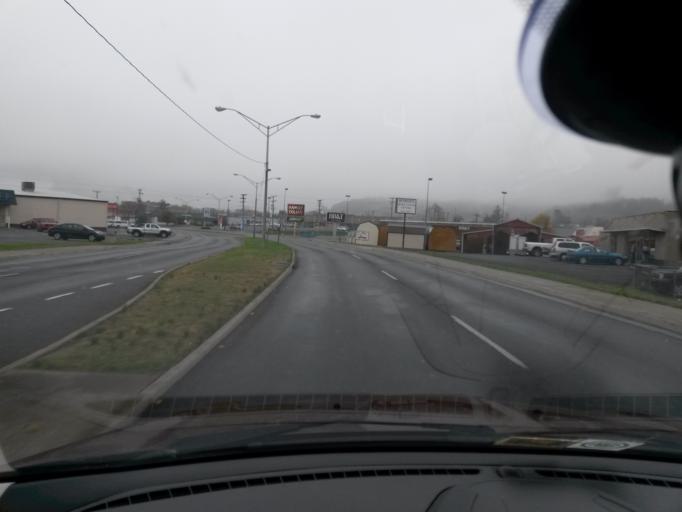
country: US
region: Virginia
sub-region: City of Covington
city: Fairlawn
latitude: 37.7795
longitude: -79.9906
